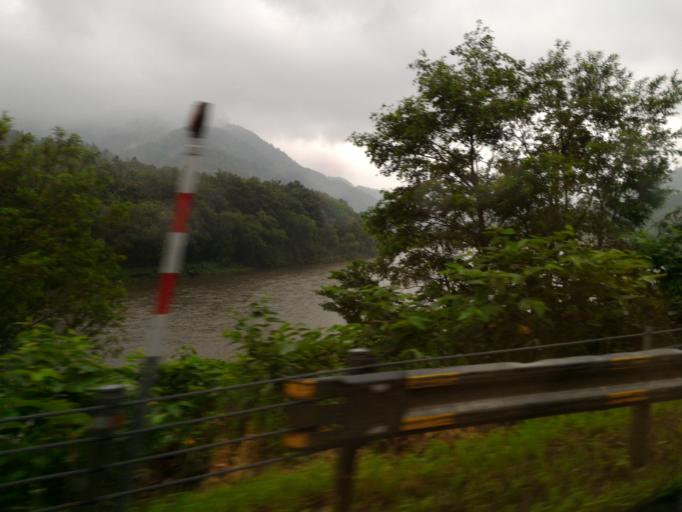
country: JP
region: Hokkaido
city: Nayoro
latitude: 44.7367
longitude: 142.1363
